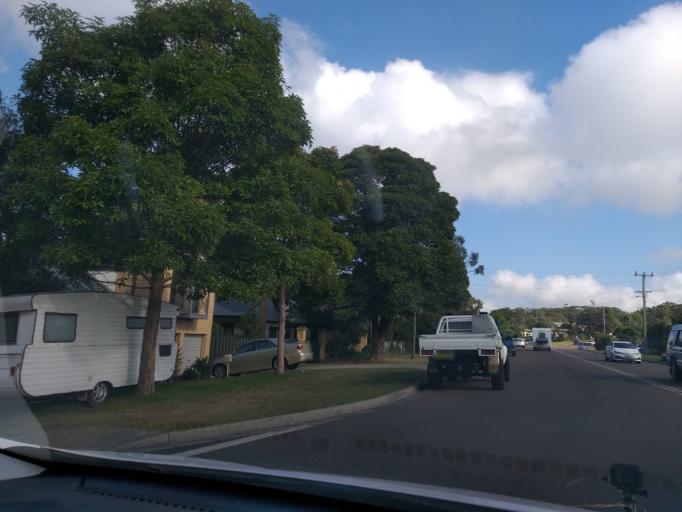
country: AU
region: New South Wales
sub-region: Wollongong
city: Helensburgh
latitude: -34.1925
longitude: 150.9772
